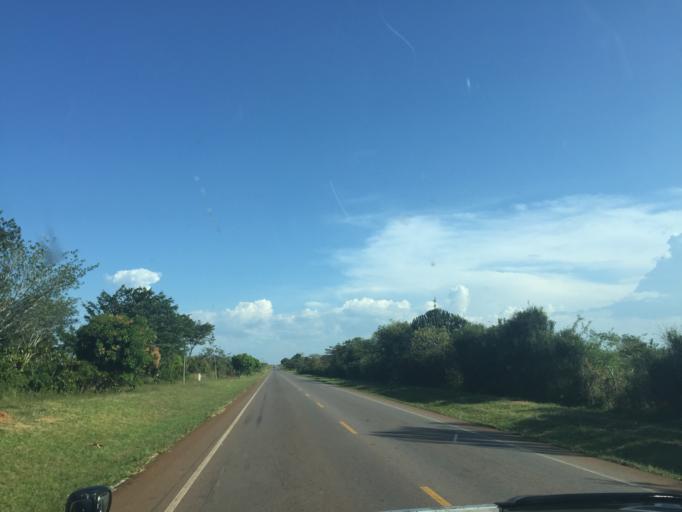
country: UG
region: Central Region
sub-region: Nakasongola District
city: Nakasongola
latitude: 1.2888
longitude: 32.4293
